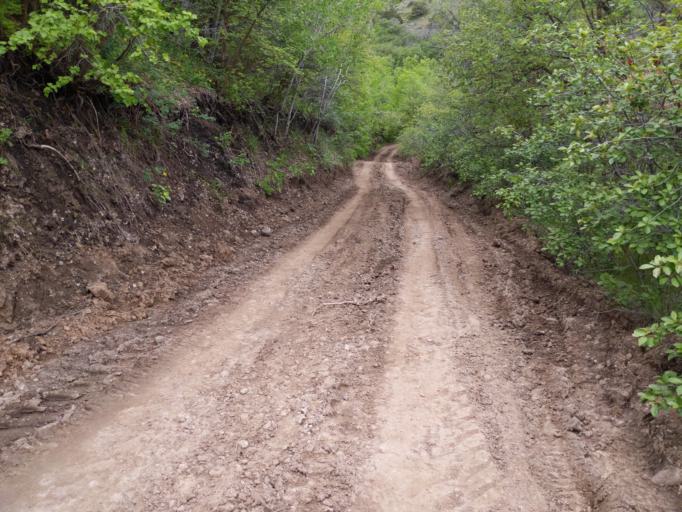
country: US
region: Idaho
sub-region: Bannock County
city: Pocatello
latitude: 42.8241
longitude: -112.4852
